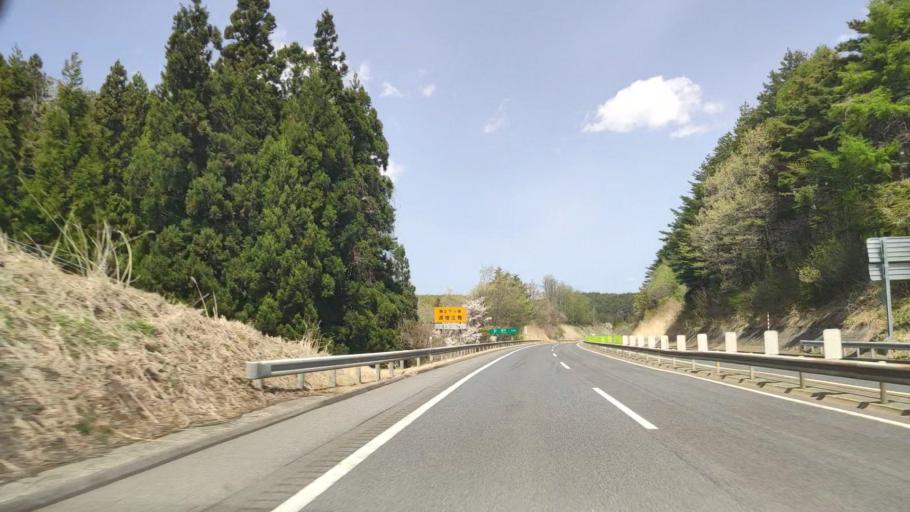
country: JP
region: Aomori
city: Hachinohe
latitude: 40.4177
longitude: 141.4406
